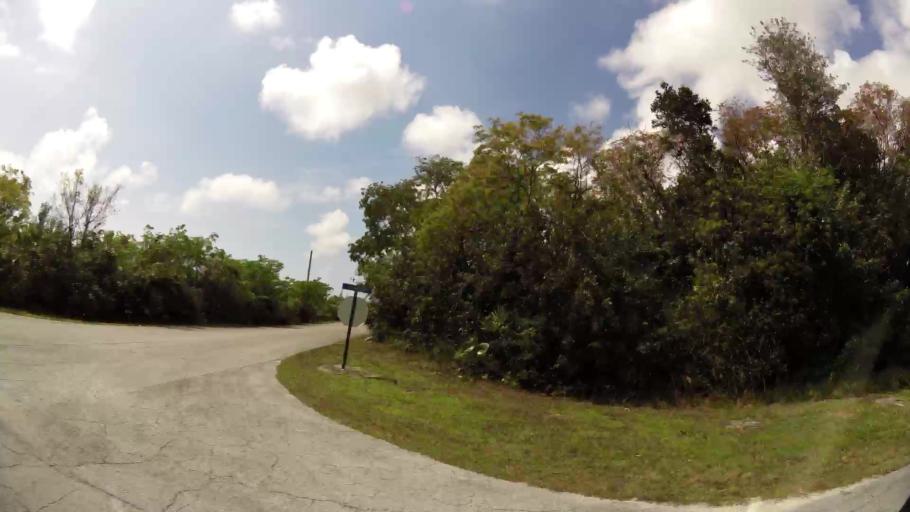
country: BS
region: Freeport
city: Freeport
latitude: 26.5114
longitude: -78.7091
